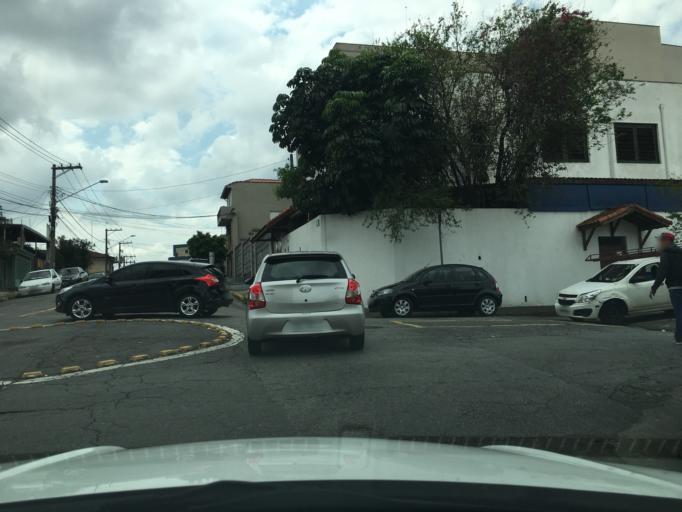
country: BR
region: Sao Paulo
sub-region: Sao Paulo
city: Sao Paulo
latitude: -23.4941
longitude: -46.6489
